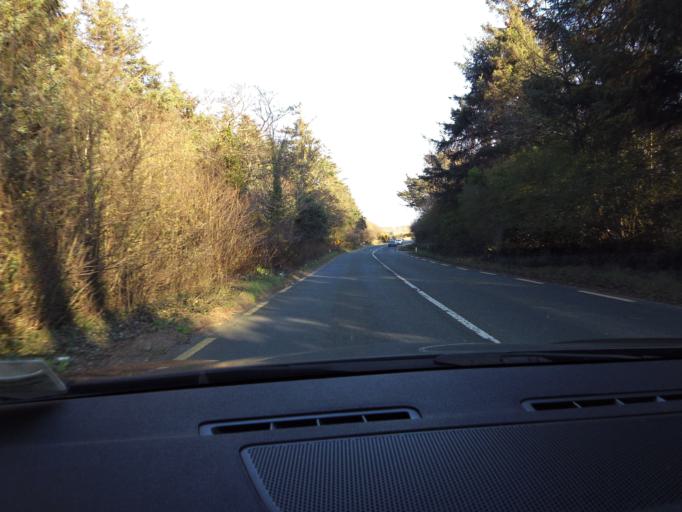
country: IE
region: Connaught
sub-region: County Galway
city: Oughterard
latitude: 53.2798
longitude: -9.5356
